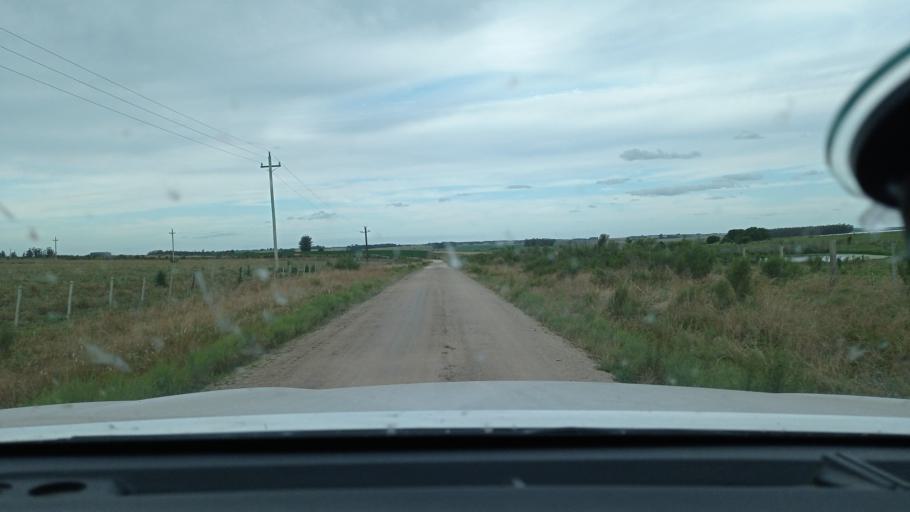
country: UY
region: Florida
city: Casupa
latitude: -34.1053
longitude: -55.7578
